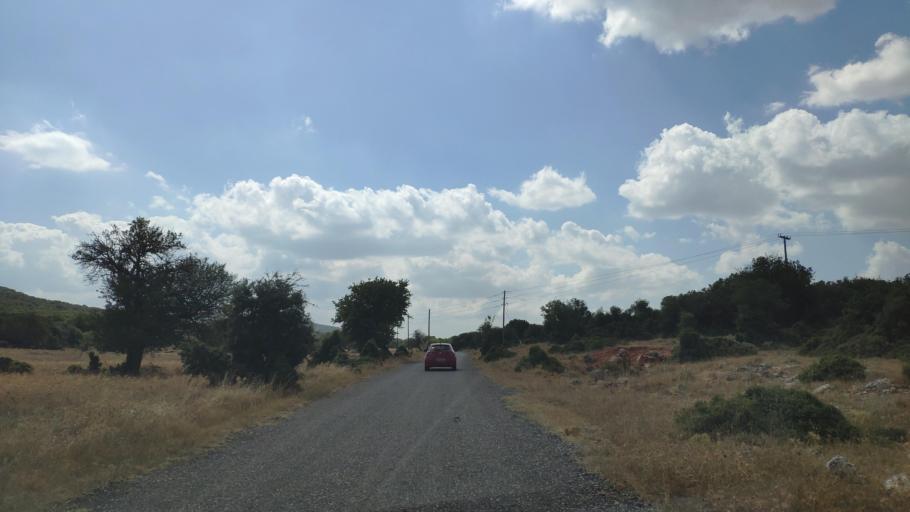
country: GR
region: Peloponnese
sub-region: Nomos Lakonias
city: Kariai
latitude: 37.3088
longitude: 22.4538
